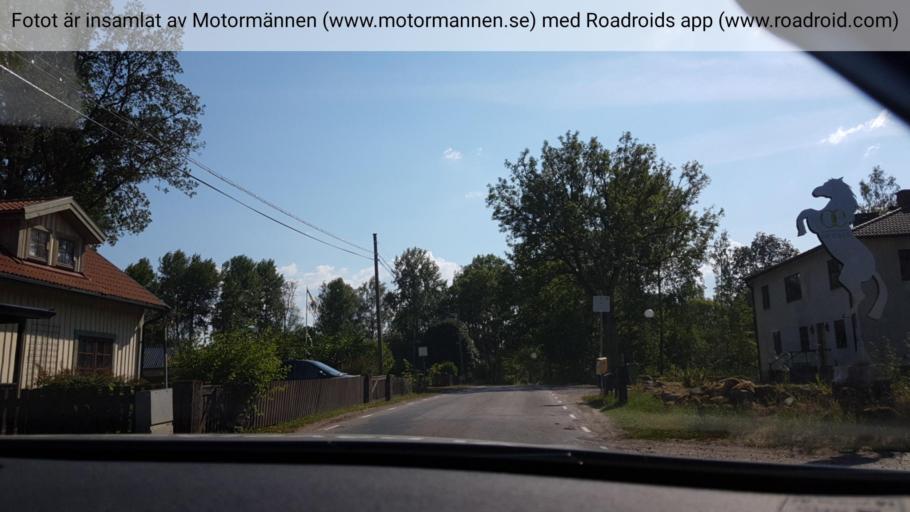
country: SE
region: Vaestra Goetaland
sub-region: Mariestads Kommun
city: Mariestad
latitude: 58.6159
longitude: 13.8798
